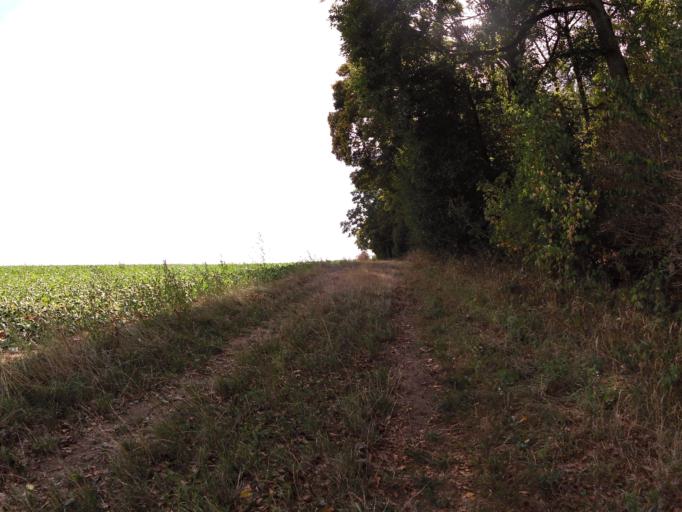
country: DE
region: Bavaria
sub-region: Regierungsbezirk Unterfranken
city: Hettstadt
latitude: 49.7912
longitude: 9.8173
